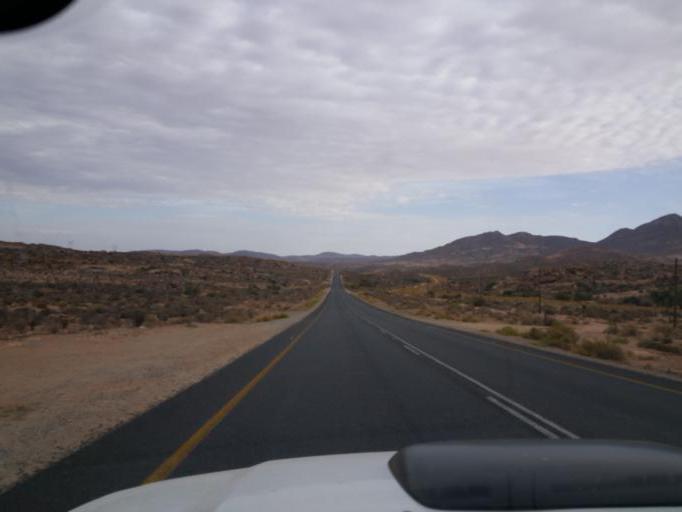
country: ZA
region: Northern Cape
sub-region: Namakwa District Municipality
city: Springbok
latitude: -29.5439
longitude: 17.8642
